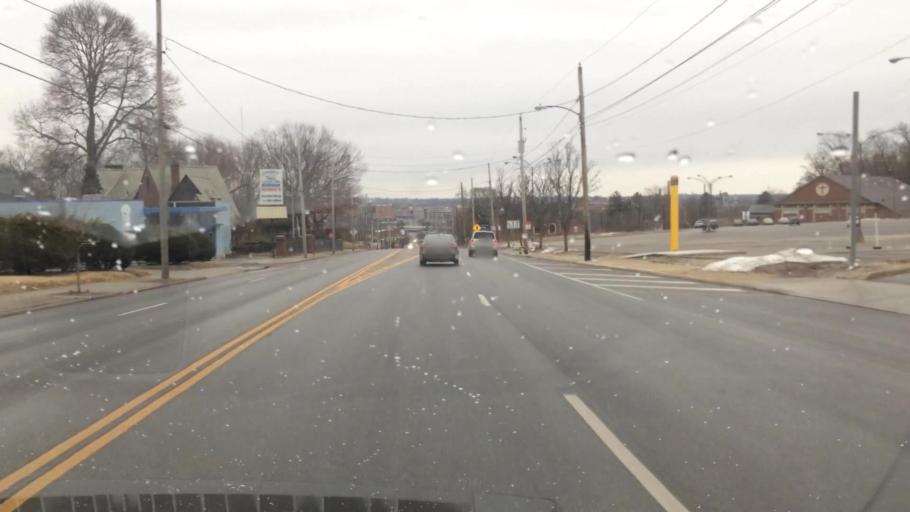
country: US
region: Ohio
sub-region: Summit County
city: Akron
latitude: 41.0889
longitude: -81.5414
